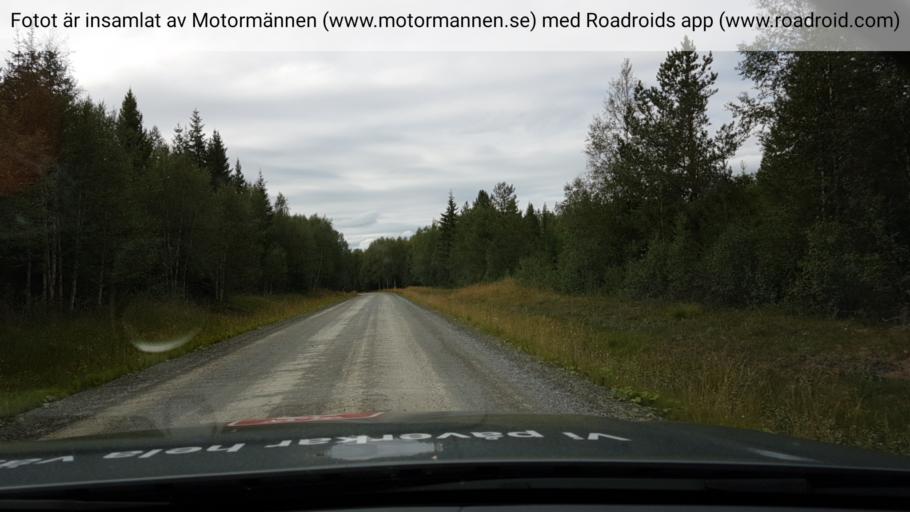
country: SE
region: Jaemtland
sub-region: Krokoms Kommun
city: Valla
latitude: 63.6628
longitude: 13.7461
